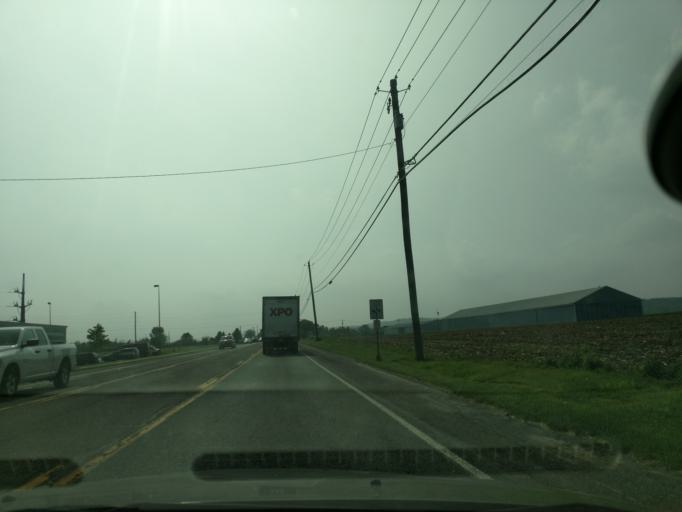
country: US
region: Pennsylvania
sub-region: Chester County
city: Elverson
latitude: 40.1561
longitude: -75.8691
